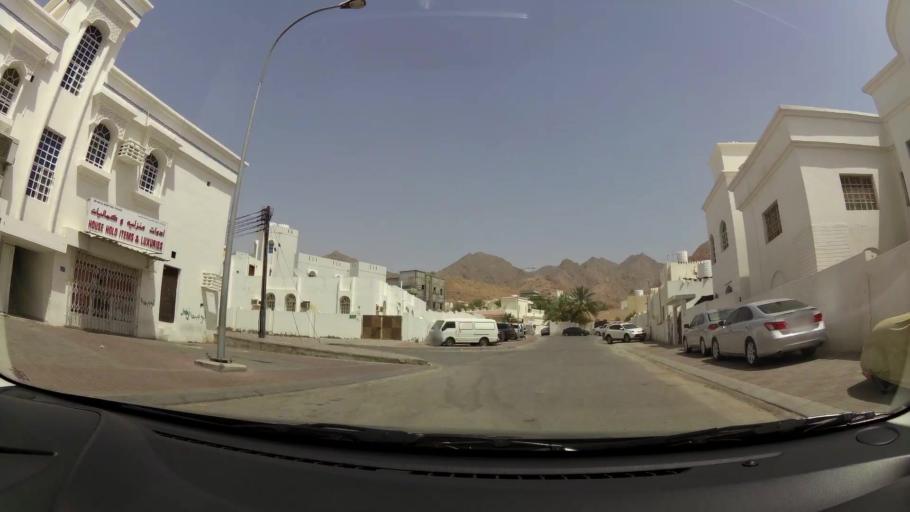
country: OM
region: Muhafazat Masqat
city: Bawshar
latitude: 23.5343
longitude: 58.3838
